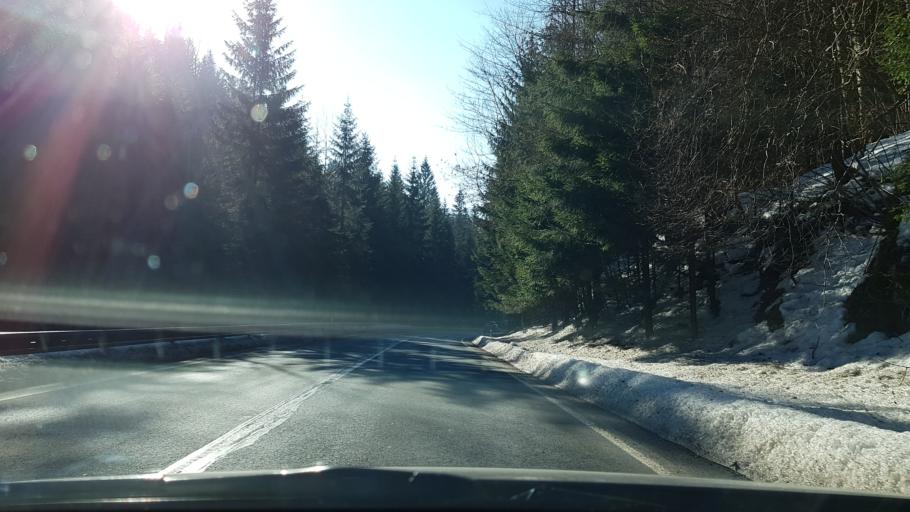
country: CZ
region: Olomoucky
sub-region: Okres Sumperk
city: Stare Mesto
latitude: 50.1426
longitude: 17.0117
